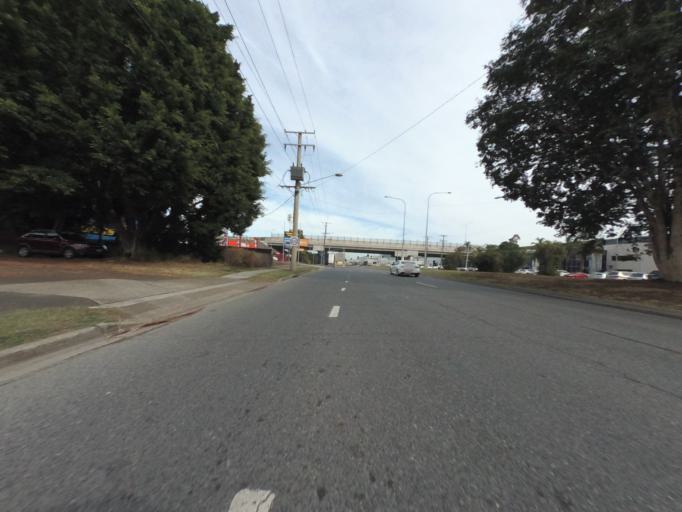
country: AU
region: Queensland
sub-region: Brisbane
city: Ascot
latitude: -27.4298
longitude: 153.0946
